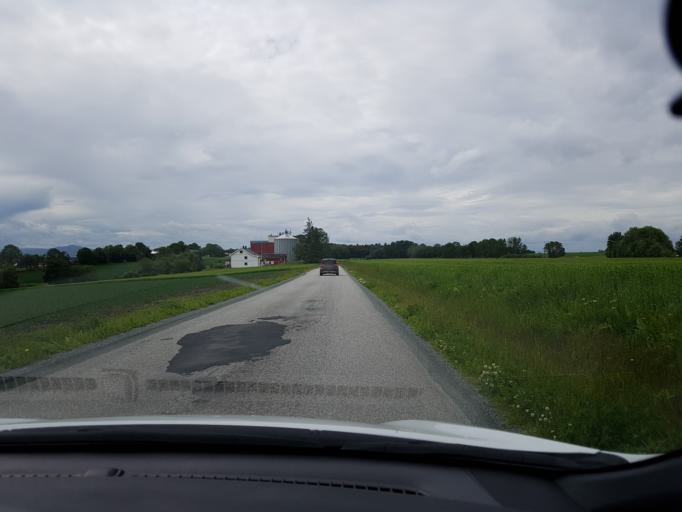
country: NO
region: Nord-Trondelag
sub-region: Frosta
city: Frosta
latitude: 63.5731
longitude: 10.7099
